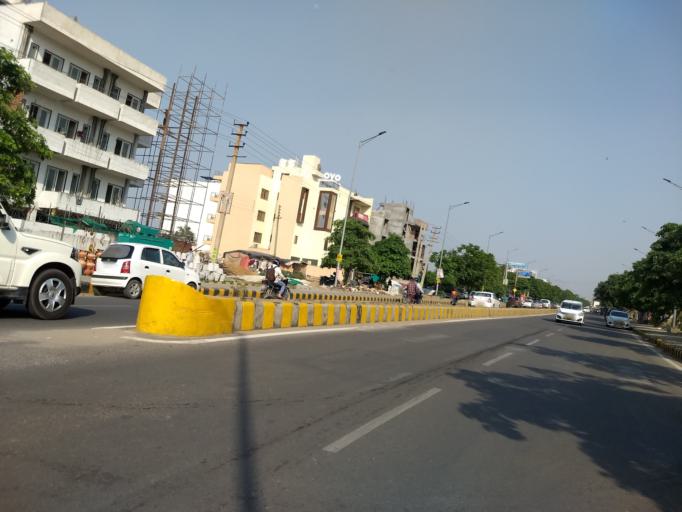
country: IN
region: Haryana
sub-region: Gurgaon
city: Gurgaon
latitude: 28.4349
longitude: 77.0697
